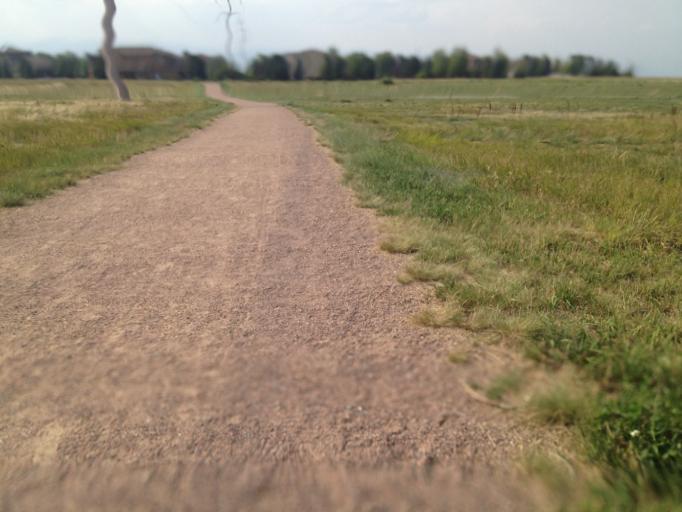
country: US
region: Colorado
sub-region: Boulder County
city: Superior
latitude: 39.9714
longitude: -105.1739
